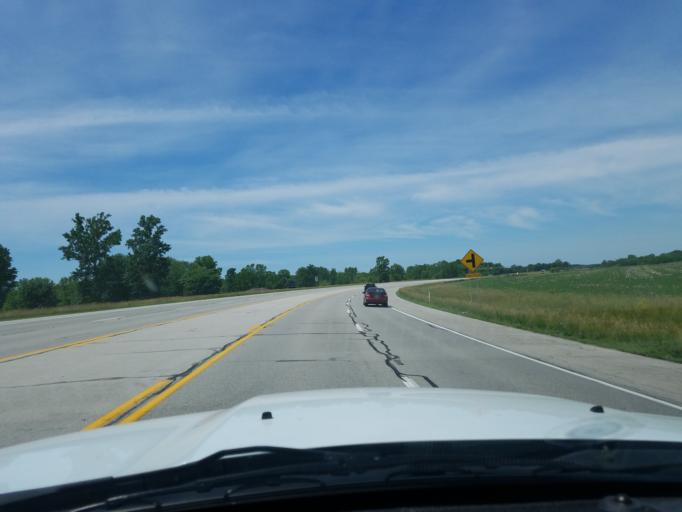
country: US
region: Indiana
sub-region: Delaware County
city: Yorktown
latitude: 40.1215
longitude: -85.4545
